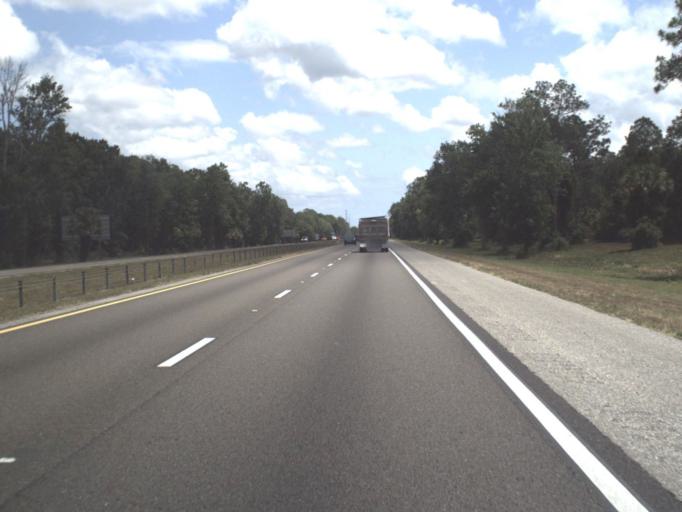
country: US
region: Florida
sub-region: Orange County
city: Wedgefield
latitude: 28.4524
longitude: -80.9998
